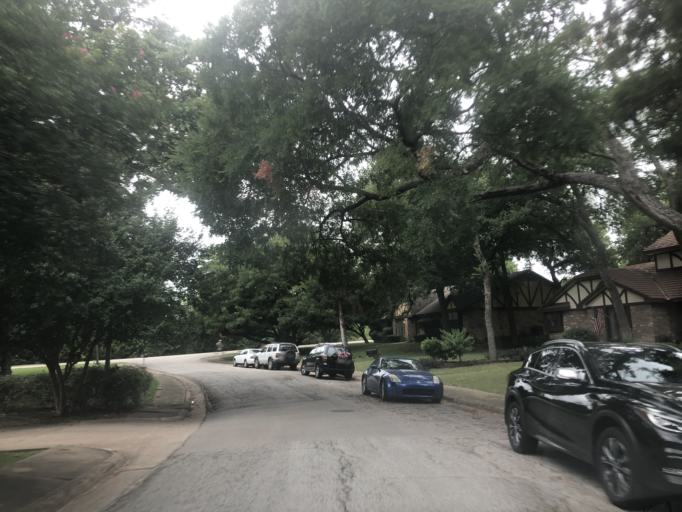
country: US
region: Texas
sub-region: Dallas County
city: Duncanville
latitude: 32.6353
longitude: -96.9177
